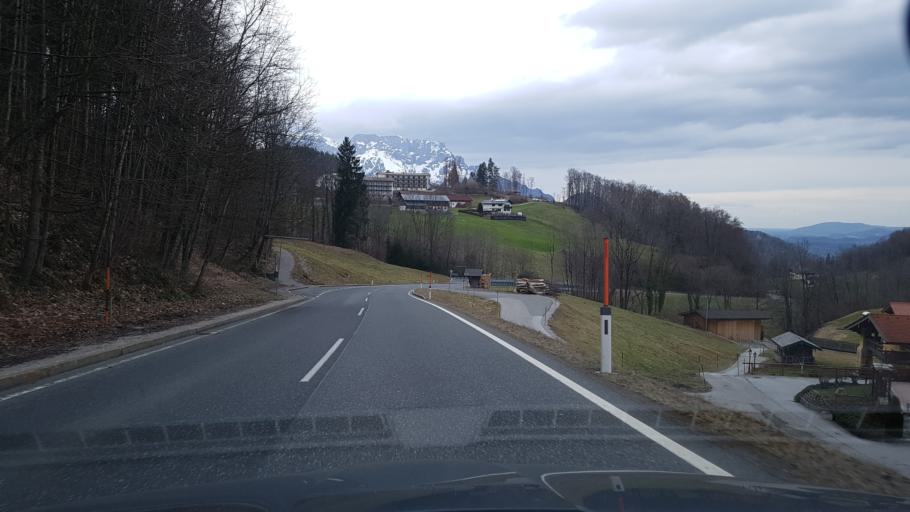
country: AT
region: Salzburg
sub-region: Politischer Bezirk Hallein
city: Hallein
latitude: 47.6615
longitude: 13.0958
